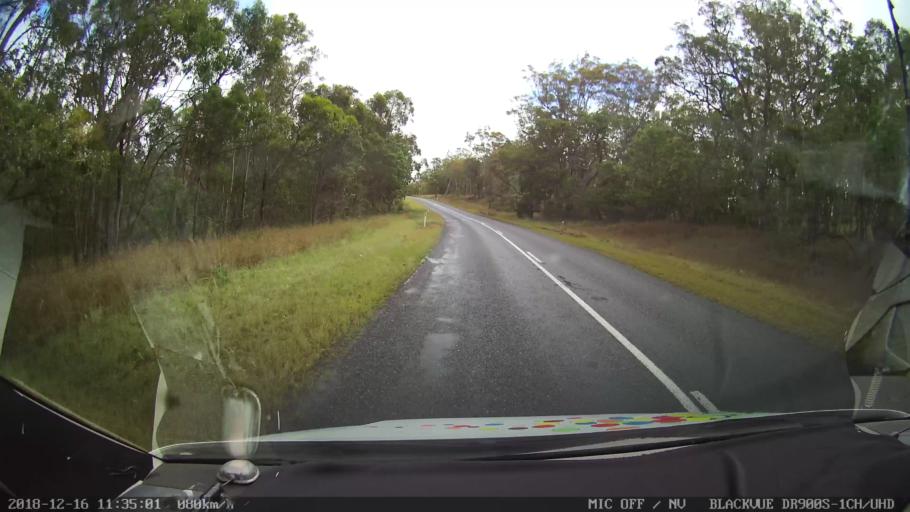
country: AU
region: New South Wales
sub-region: Tenterfield Municipality
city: Carrolls Creek
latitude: -28.9944
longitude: 152.1595
